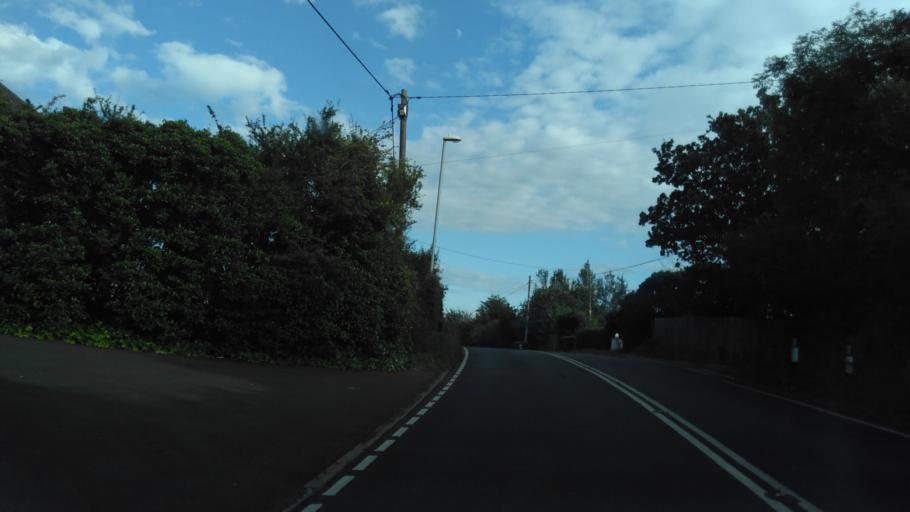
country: GB
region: England
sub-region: Kent
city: Blean
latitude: 51.3234
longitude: 1.0267
